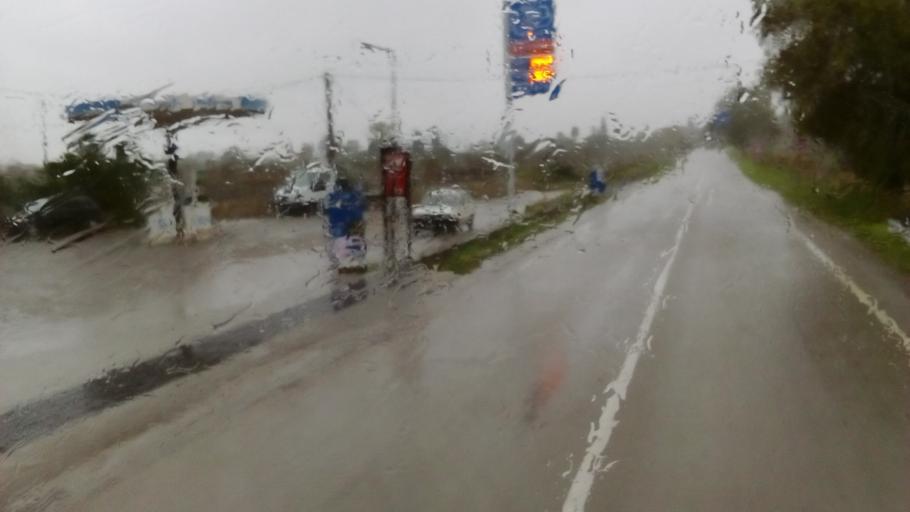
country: IT
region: Sicily
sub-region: Enna
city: Pietraperzia
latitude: 37.4217
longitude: 14.1722
